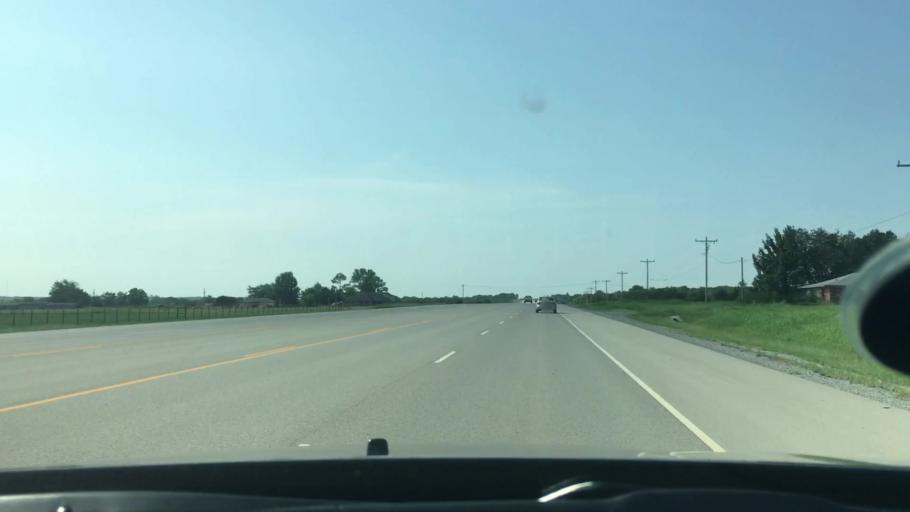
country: US
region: Oklahoma
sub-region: Bryan County
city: Durant
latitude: 34.0739
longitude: -96.3733
